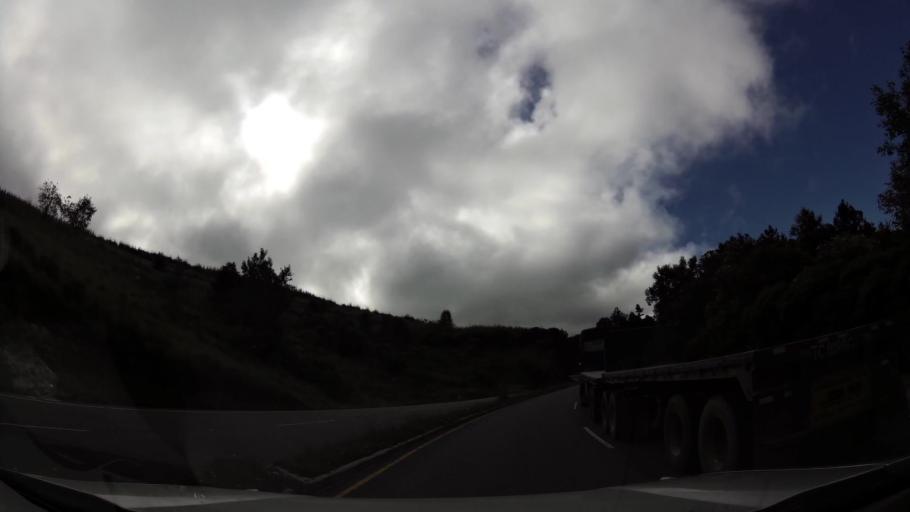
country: GT
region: Quetzaltenango
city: Salcaja
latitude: 14.8628
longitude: -91.4083
